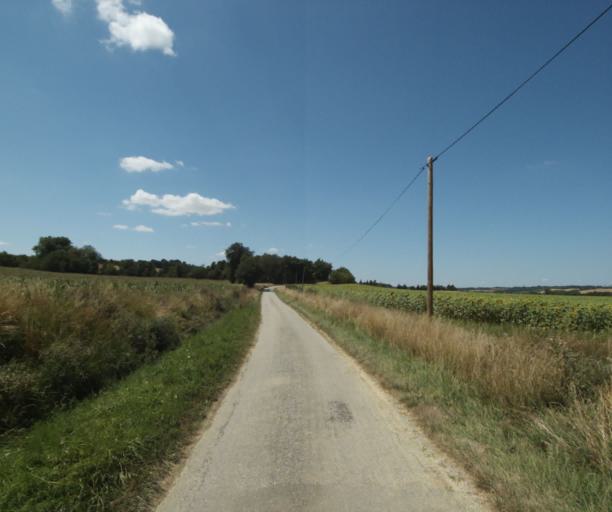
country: FR
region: Midi-Pyrenees
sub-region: Departement de la Haute-Garonne
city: Saint-Felix-Lauragais
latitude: 43.4719
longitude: 1.8846
